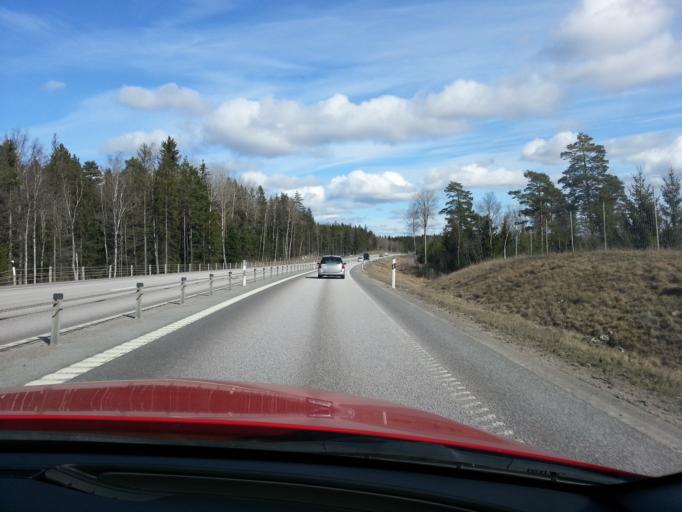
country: SE
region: Uppsala
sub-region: Uppsala Kommun
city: Storvreta
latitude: 59.9214
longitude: 17.7628
